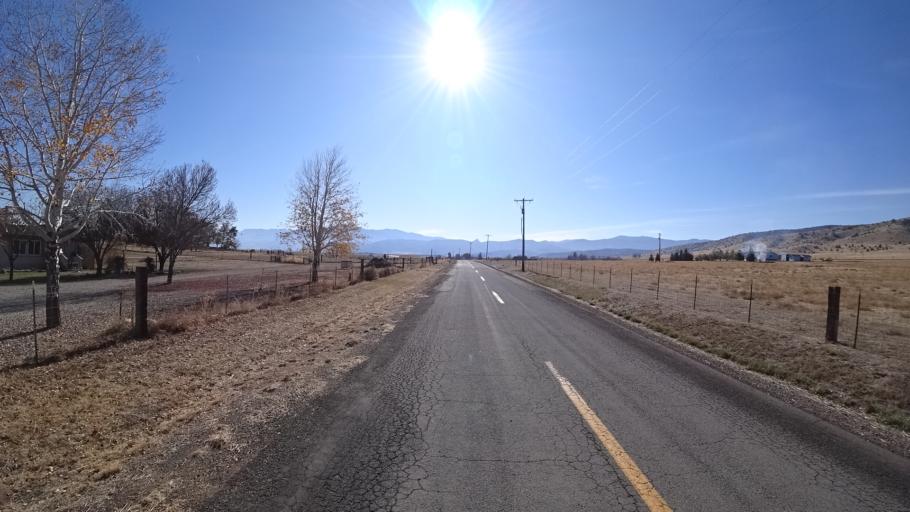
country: US
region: California
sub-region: Siskiyou County
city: Montague
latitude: 41.5804
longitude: -122.5459
